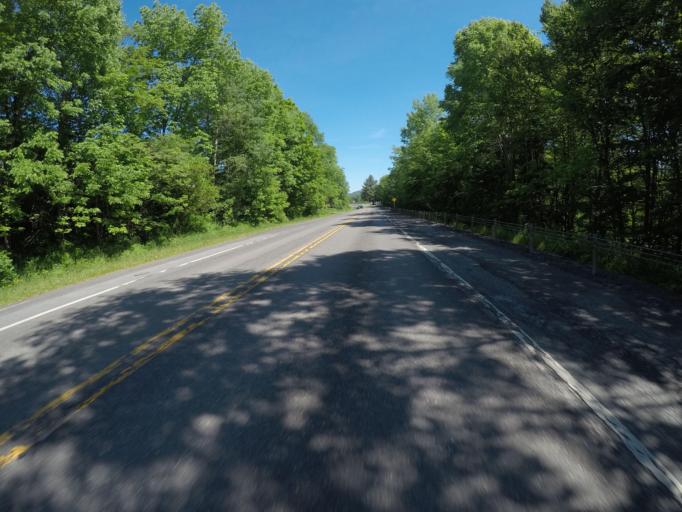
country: US
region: New York
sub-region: Delaware County
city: Delhi
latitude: 42.2184
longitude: -74.9675
